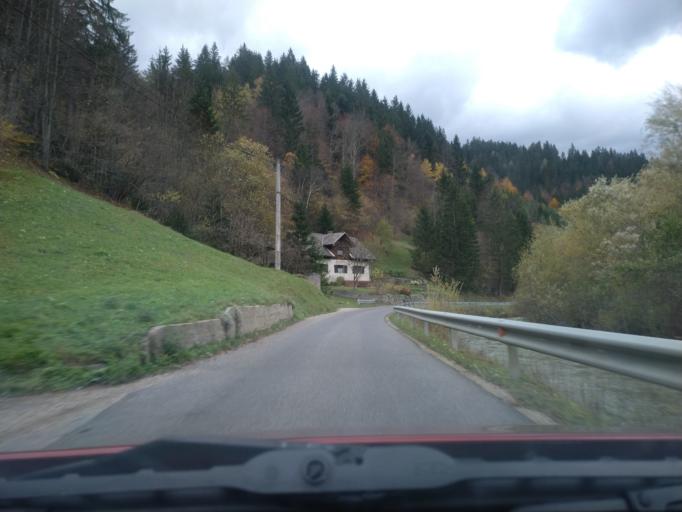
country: SI
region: Luce
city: Luce
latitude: 46.3440
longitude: 14.7298
